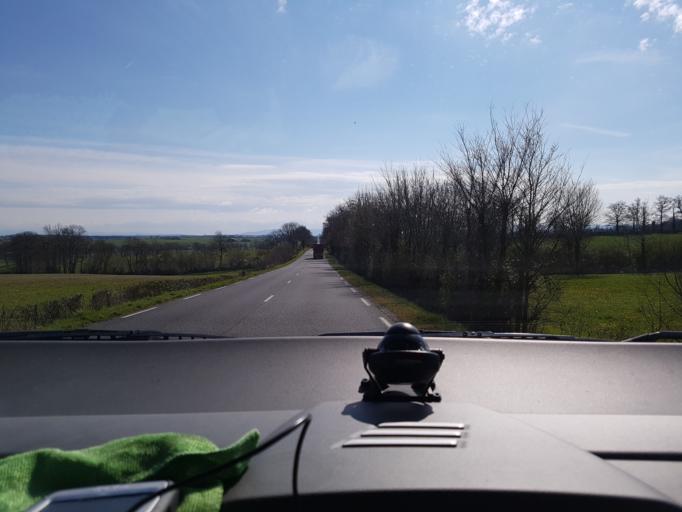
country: FR
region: Midi-Pyrenees
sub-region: Departement de l'Aveyron
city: Druelle
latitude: 44.3698
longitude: 2.4808
